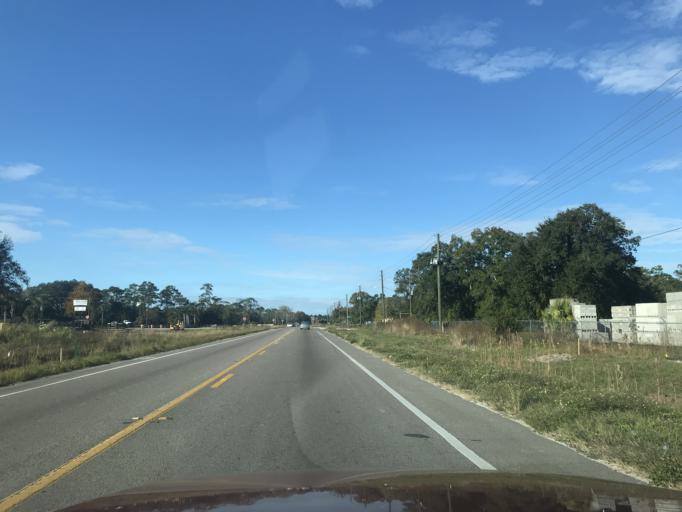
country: US
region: Florida
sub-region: Osceola County
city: Campbell
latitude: 28.2555
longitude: -81.4725
